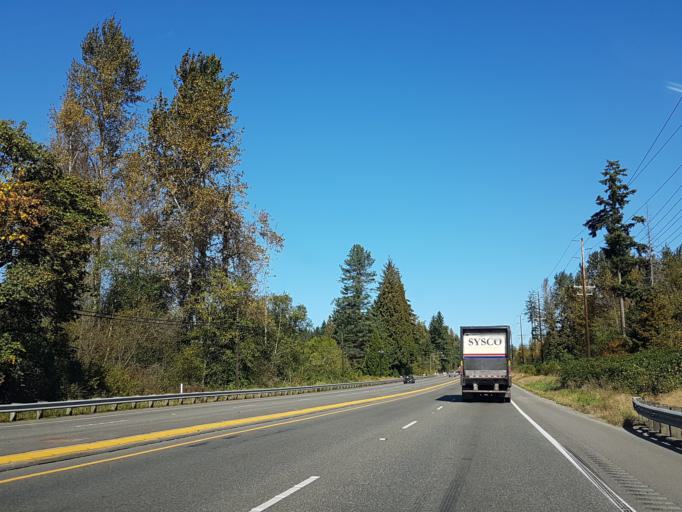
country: US
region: Washington
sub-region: Snohomish County
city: Maltby
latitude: 47.7937
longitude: -122.1433
